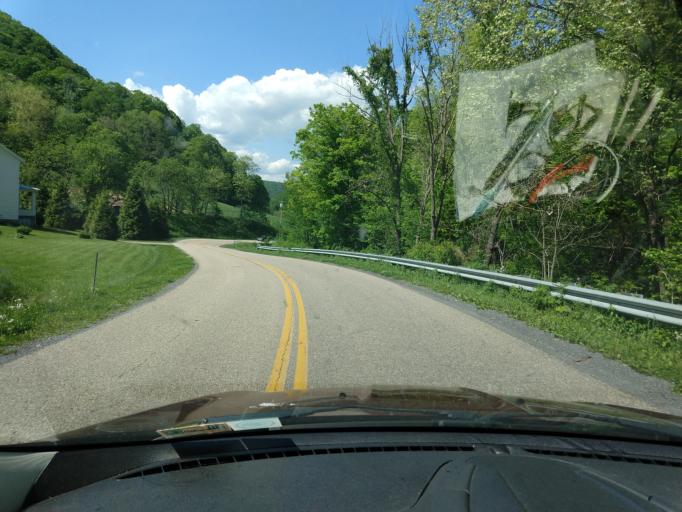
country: US
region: Virginia
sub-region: City of Covington
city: Fairlawn
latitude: 37.7377
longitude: -79.9126
